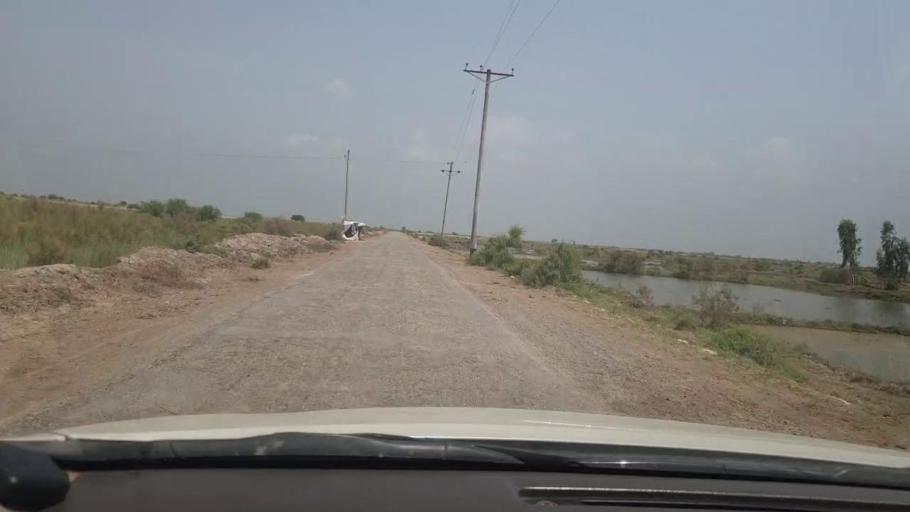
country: PK
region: Sindh
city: Garhi Yasin
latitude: 28.0065
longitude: 68.4997
